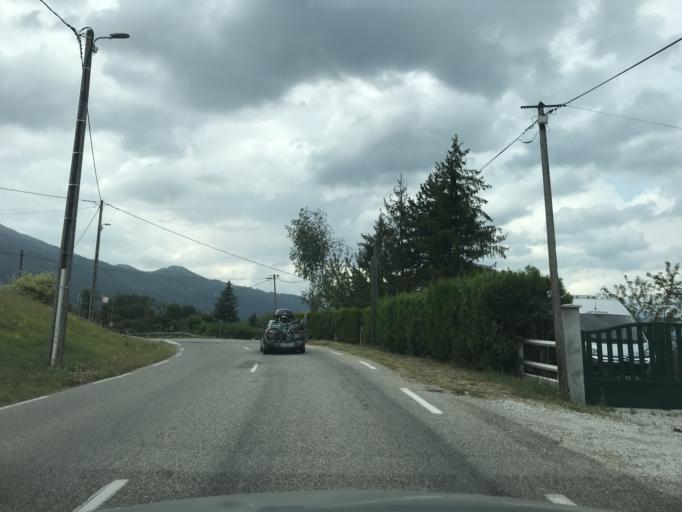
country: FR
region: Rhone-Alpes
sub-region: Departement de la Savoie
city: Brison-Saint-Innocent
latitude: 45.7335
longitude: 5.8851
